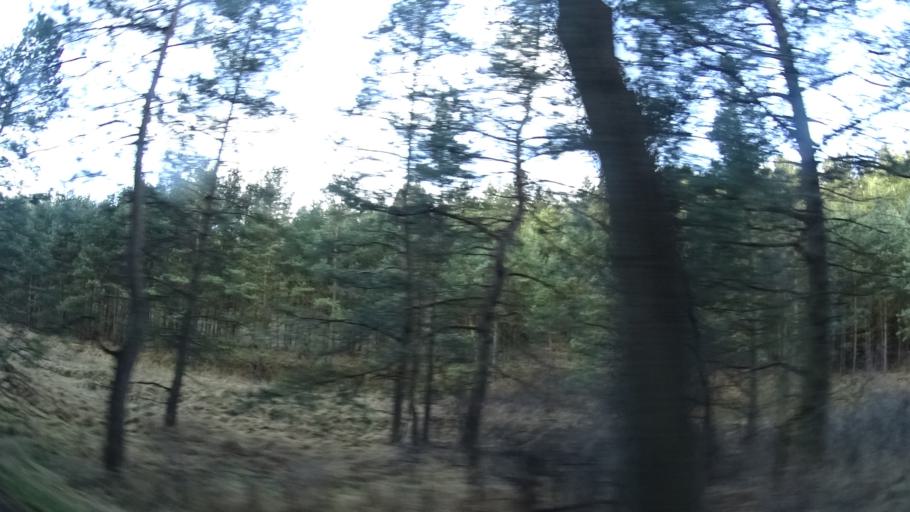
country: DE
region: Thuringia
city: Gossel
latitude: 50.8115
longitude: 10.8528
